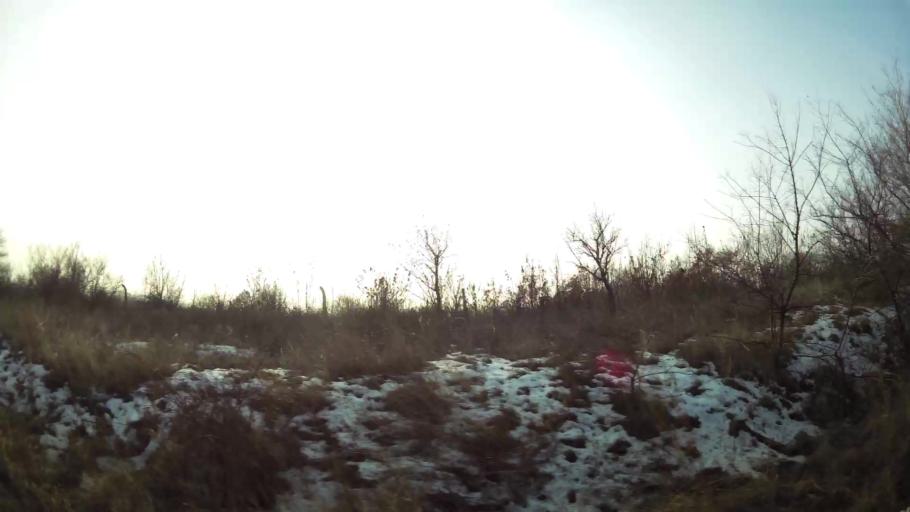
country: MK
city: Miladinovci
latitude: 41.9757
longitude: 21.6312
